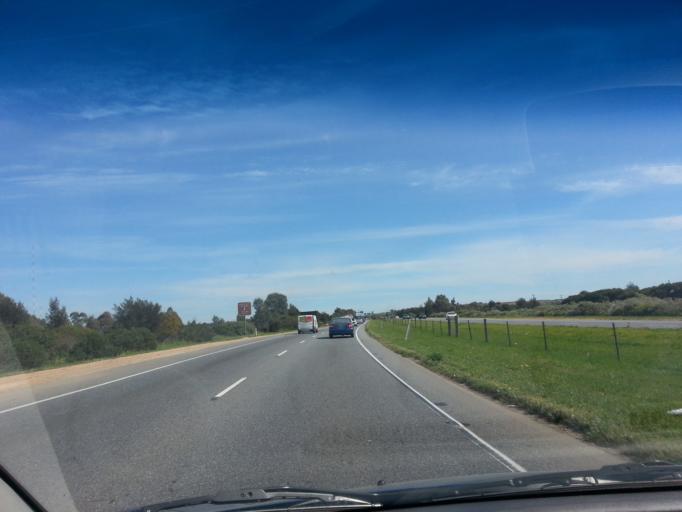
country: AU
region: South Australia
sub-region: Port Adelaide Enfield
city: Enfield
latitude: -34.8329
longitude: 138.5795
